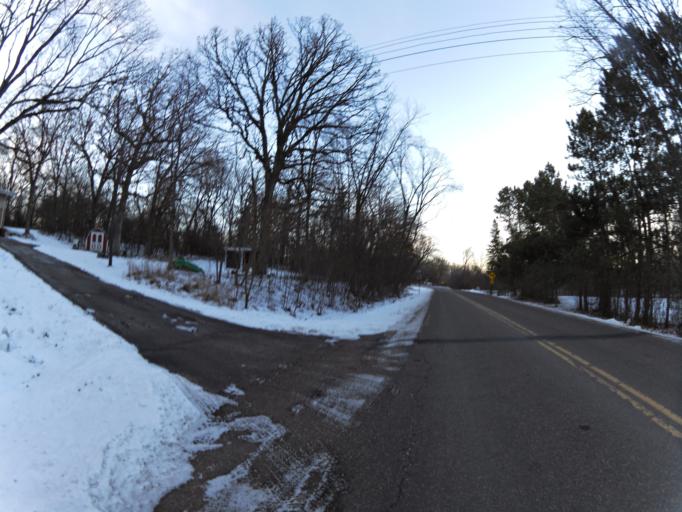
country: US
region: Minnesota
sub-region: Washington County
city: Lake Elmo
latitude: 44.9766
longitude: -92.8379
